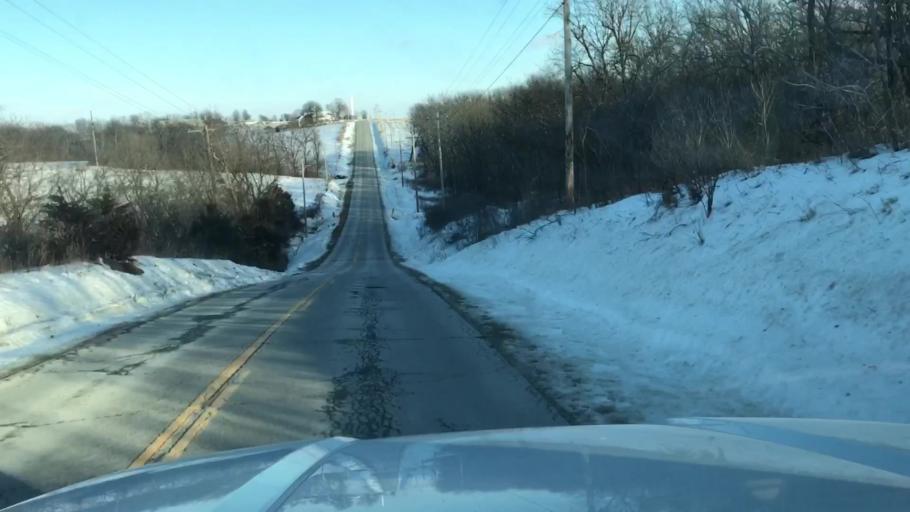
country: US
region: Missouri
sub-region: Andrew County
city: Savannah
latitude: 40.0246
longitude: -94.8932
